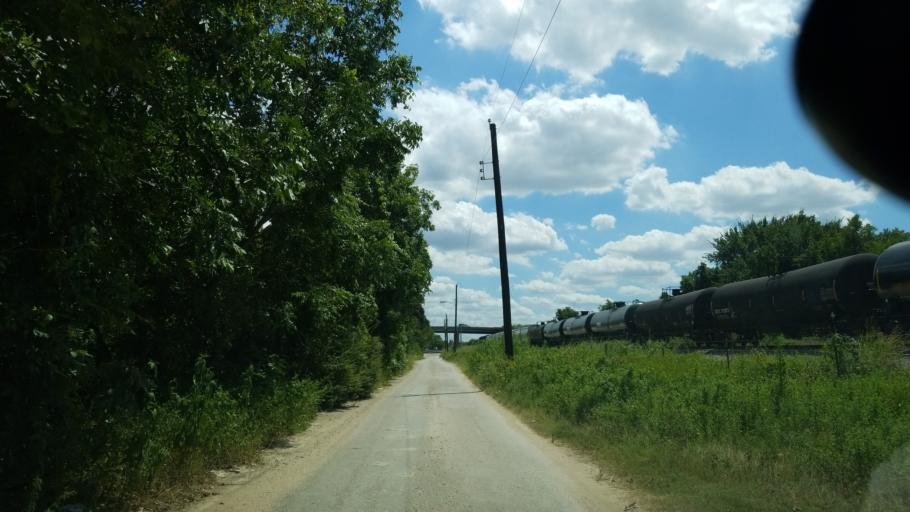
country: US
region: Texas
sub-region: Dallas County
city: Dallas
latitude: 32.7494
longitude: -96.7483
